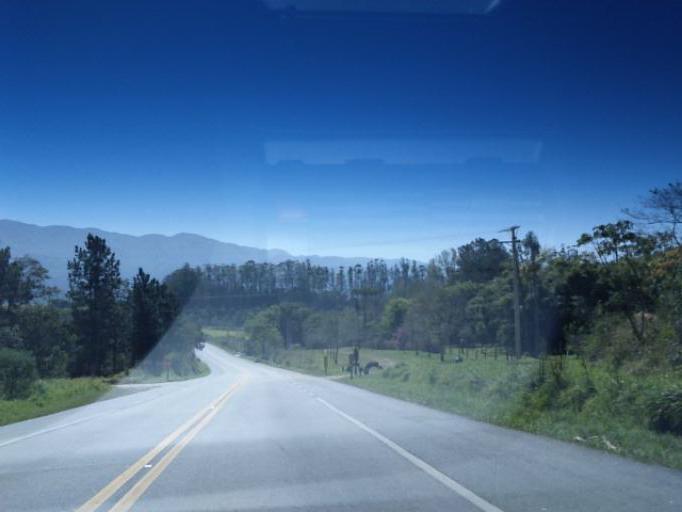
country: BR
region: Sao Paulo
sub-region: Tremembe
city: Tremembe
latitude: -22.8721
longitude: -45.5960
